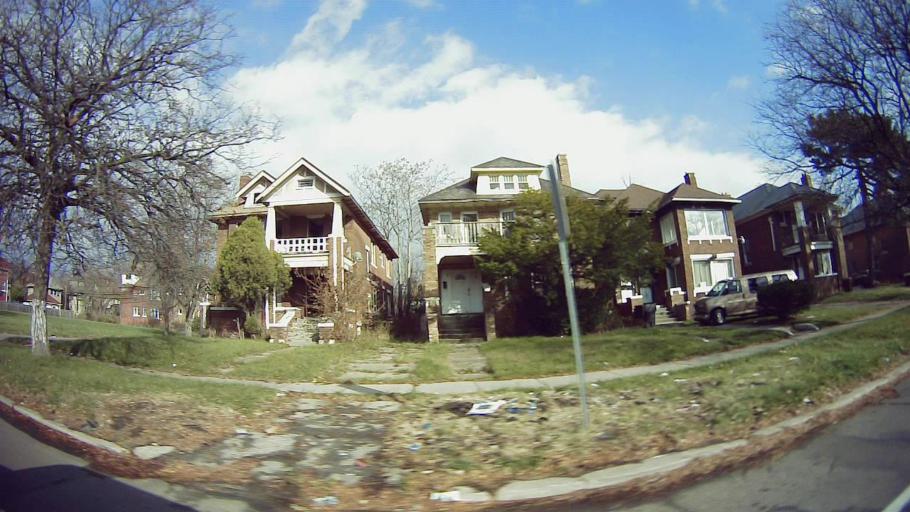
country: US
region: Michigan
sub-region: Wayne County
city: Highland Park
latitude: 42.3661
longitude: -83.1148
